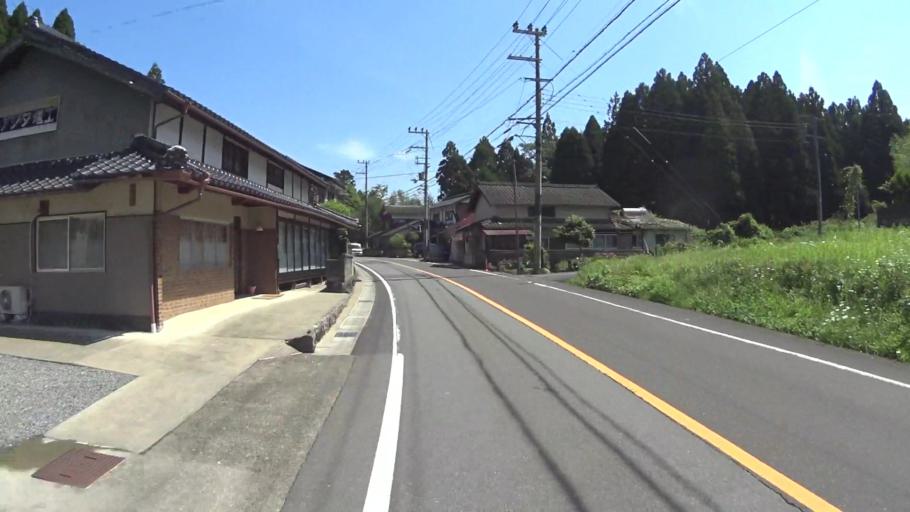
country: JP
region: Kyoto
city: Ayabe
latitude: 35.3035
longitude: 135.3148
